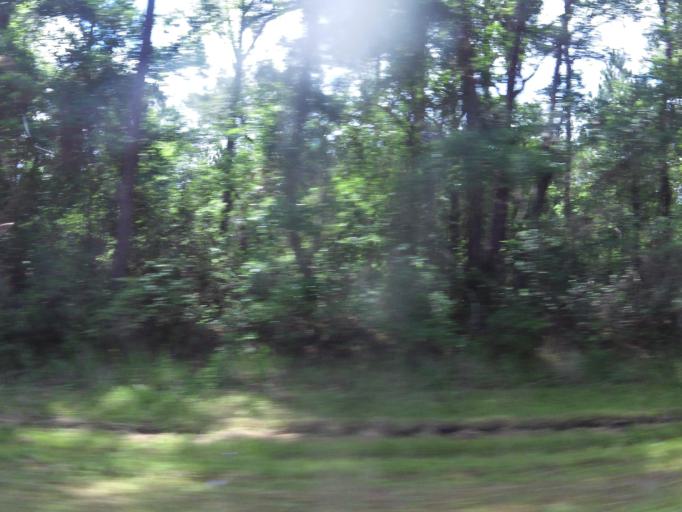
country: US
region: Florida
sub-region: Clay County
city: Green Cove Springs
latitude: 29.9214
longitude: -81.7591
